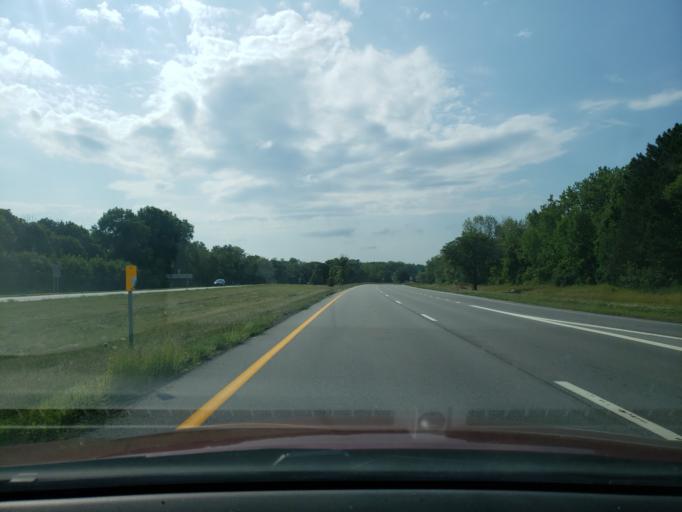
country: US
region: New York
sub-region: Monroe County
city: Irondequoit
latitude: 43.2560
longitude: -77.6308
